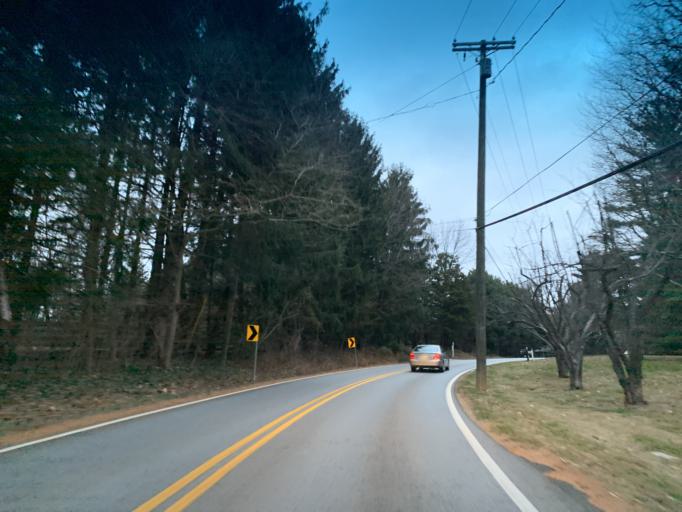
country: US
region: Maryland
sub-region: Baltimore County
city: Hampton
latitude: 39.4876
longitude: -76.5275
